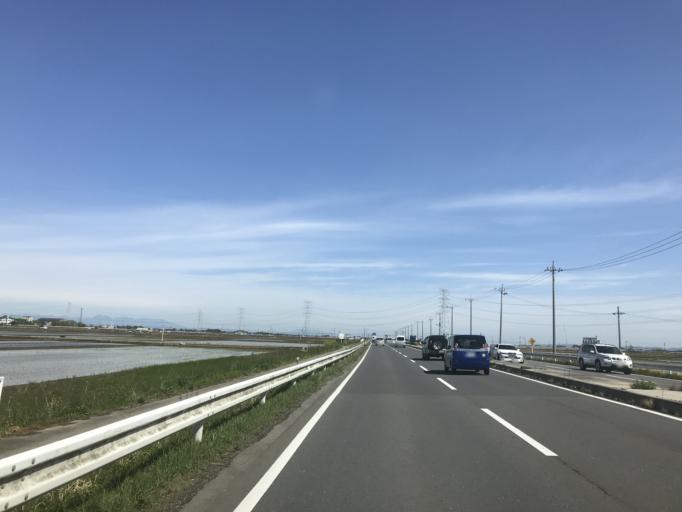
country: JP
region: Ibaraki
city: Ishige
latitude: 36.1155
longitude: 139.9832
